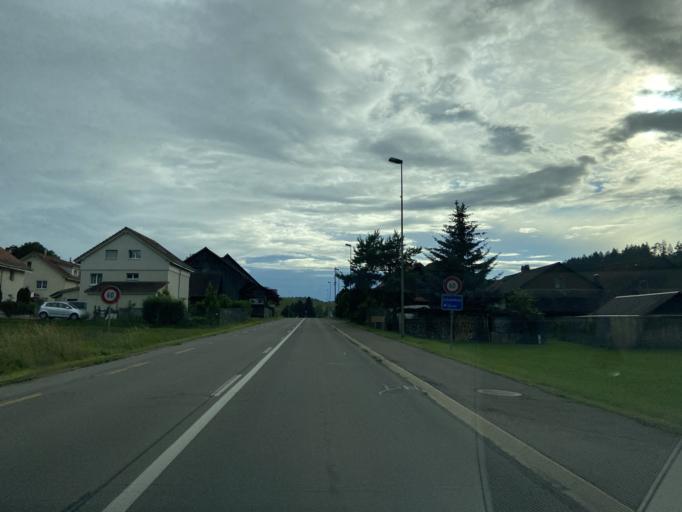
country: CH
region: Zurich
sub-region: Bezirk Winterthur
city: Elsau-Raeterschen
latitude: 47.5023
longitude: 8.8206
